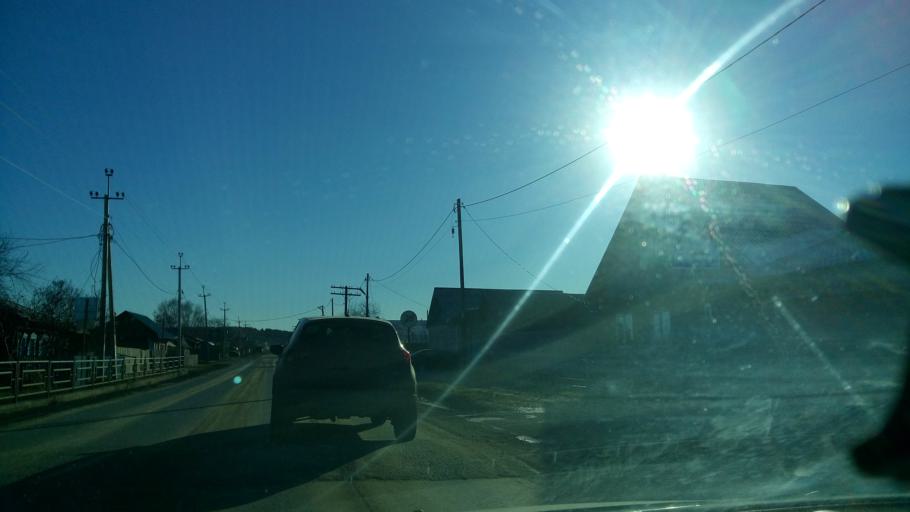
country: RU
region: Sverdlovsk
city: Gornyy Shchit
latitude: 56.6938
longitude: 60.5159
